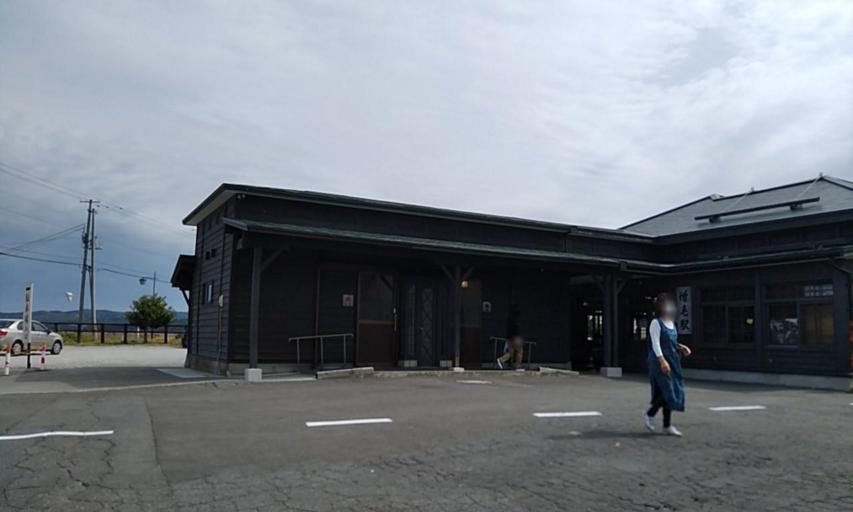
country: JP
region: Hokkaido
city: Rumoi
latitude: 43.8572
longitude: 141.5269
